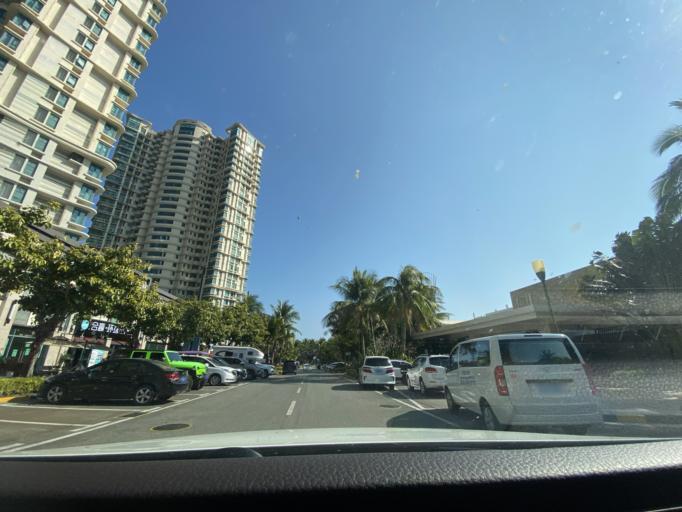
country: CN
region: Hainan
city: Yingzhou
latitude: 18.4101
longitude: 109.8749
